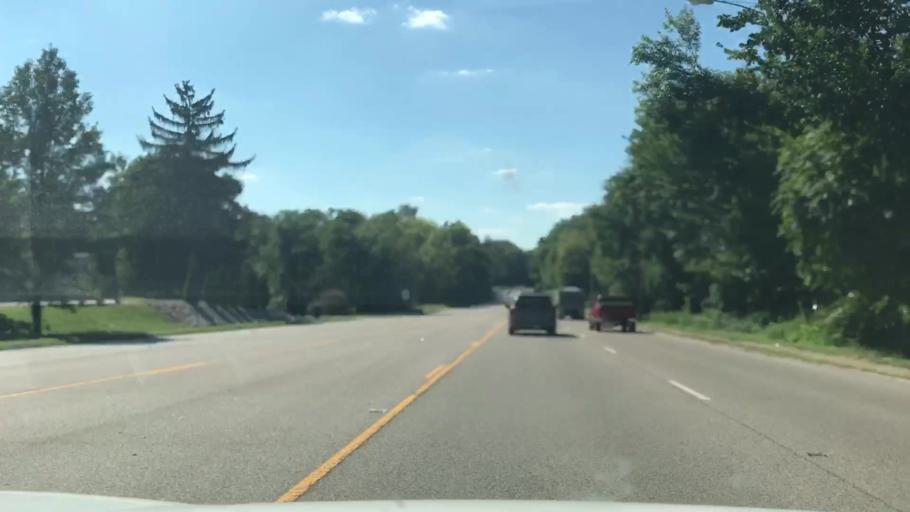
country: US
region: Illinois
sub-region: Saint Clair County
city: Swansea
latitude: 38.5419
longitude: -90.0418
